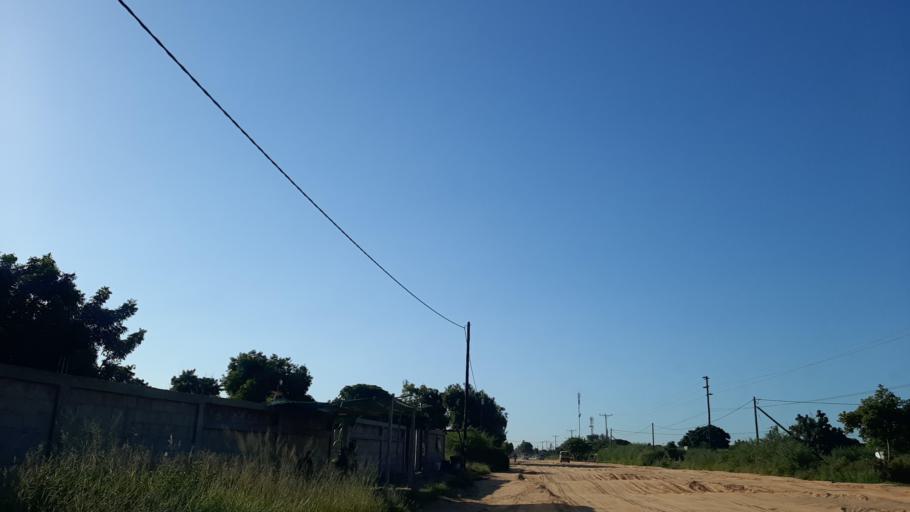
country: MZ
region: Maputo City
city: Maputo
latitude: -25.7437
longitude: 32.5428
